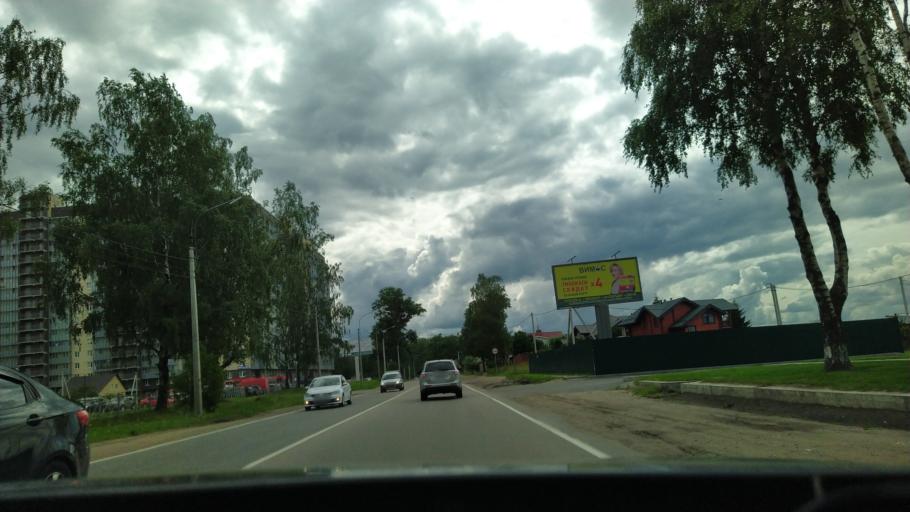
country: RU
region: Leningrad
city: Kirovsk
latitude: 59.8808
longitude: 30.9828
